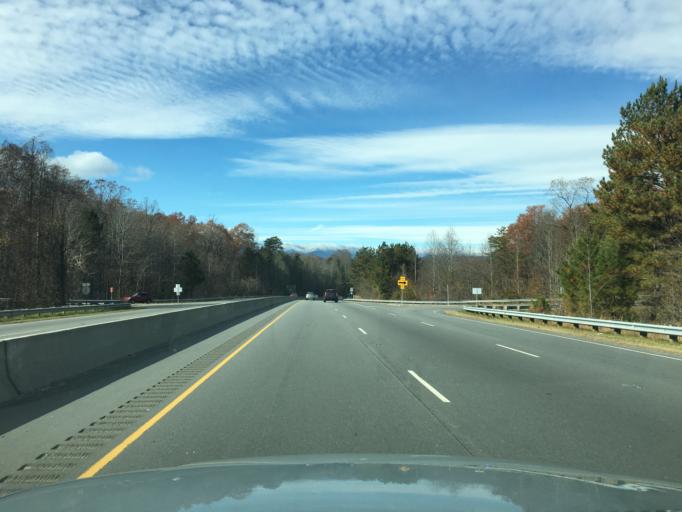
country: US
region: North Carolina
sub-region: McDowell County
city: Marion
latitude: 35.6777
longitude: -82.0242
